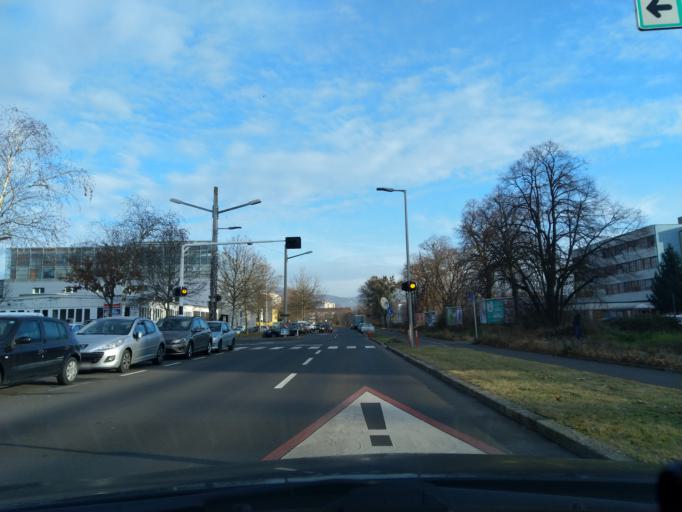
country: AT
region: Upper Austria
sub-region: Linz Stadt
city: Linz
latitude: 48.3159
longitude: 14.2877
